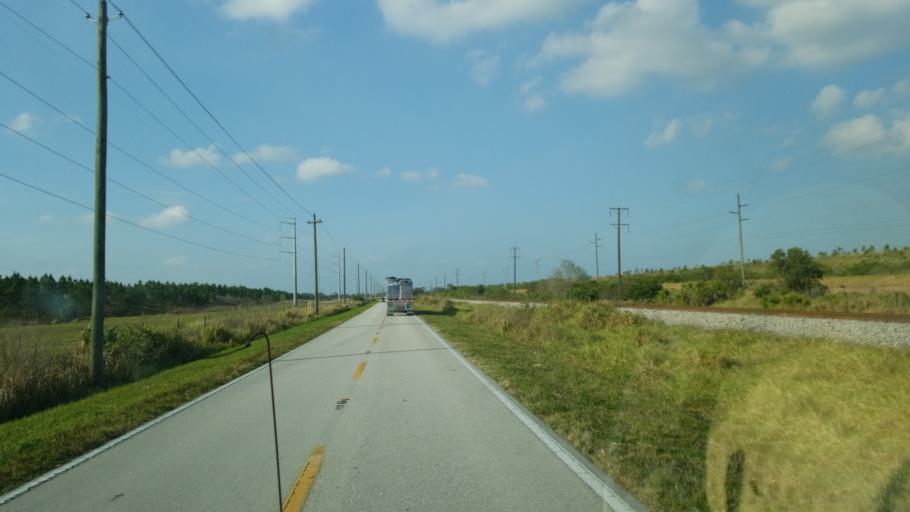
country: US
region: Florida
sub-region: Hardee County
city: Bowling Green
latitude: 27.7067
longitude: -81.9596
